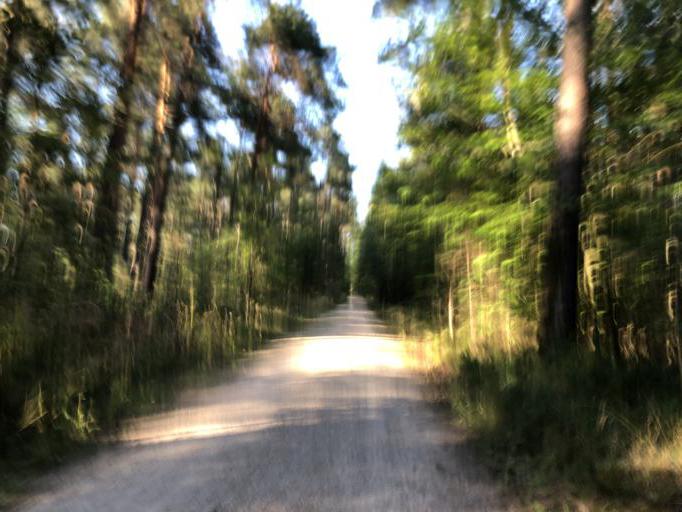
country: DE
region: Bavaria
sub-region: Regierungsbezirk Mittelfranken
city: Kalchreuth
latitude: 49.5588
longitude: 11.0979
